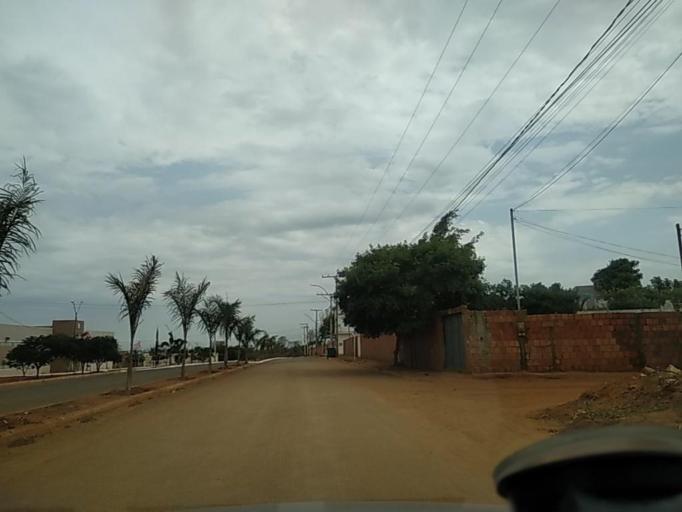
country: BR
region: Bahia
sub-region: Caetite
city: Caetite
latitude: -14.0532
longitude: -42.4726
